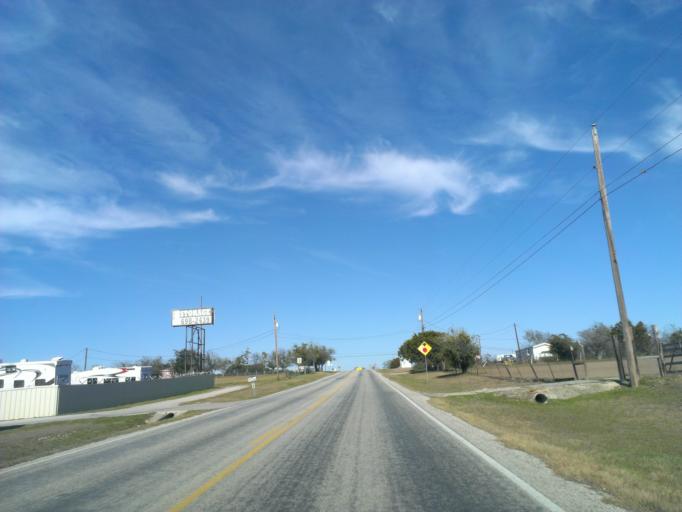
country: US
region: Texas
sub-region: Bell County
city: Nolanville
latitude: 31.0868
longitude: -97.6072
